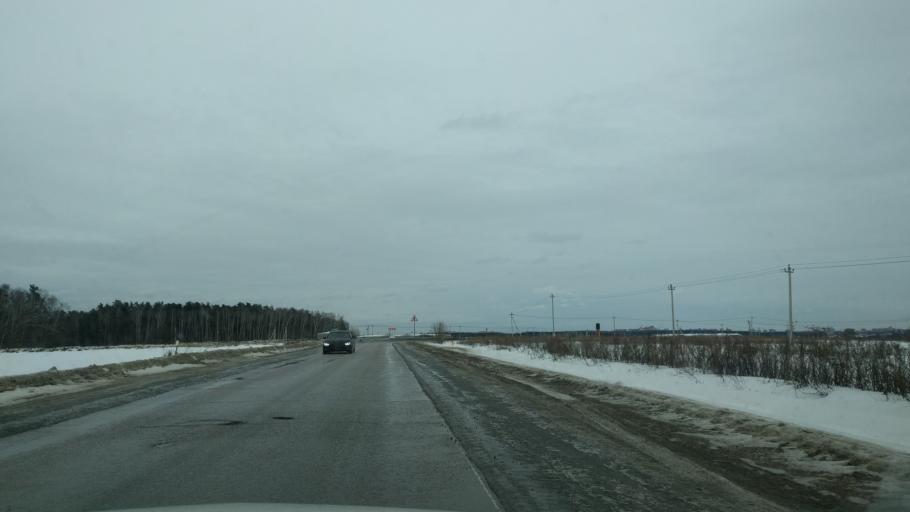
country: RU
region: Moskovskaya
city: Dubrovitsy
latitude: 55.4345
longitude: 37.4413
